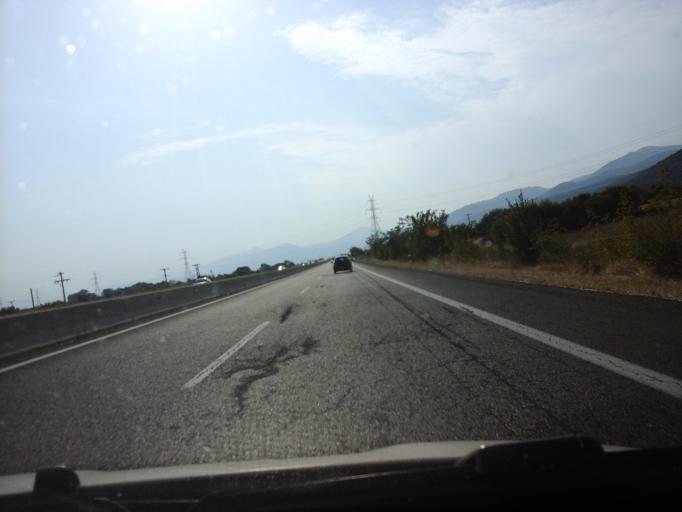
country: GR
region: East Macedonia and Thrace
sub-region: Nomos Rodopis
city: Iasmos
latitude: 41.1173
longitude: 25.1050
